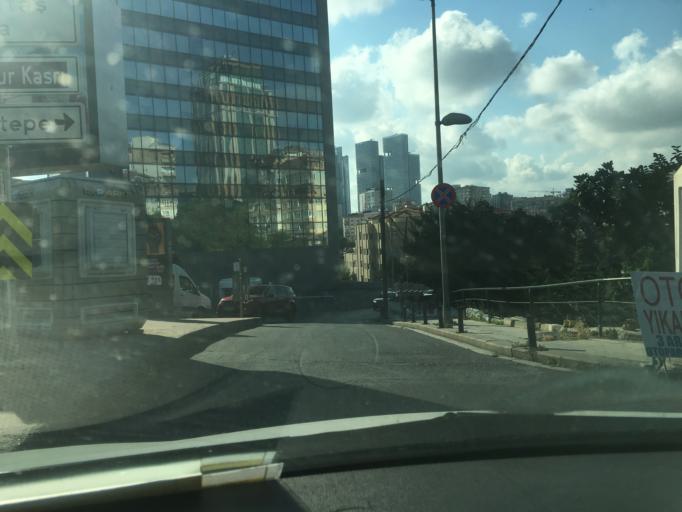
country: TR
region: Istanbul
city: Sisli
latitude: 41.0585
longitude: 29.0085
